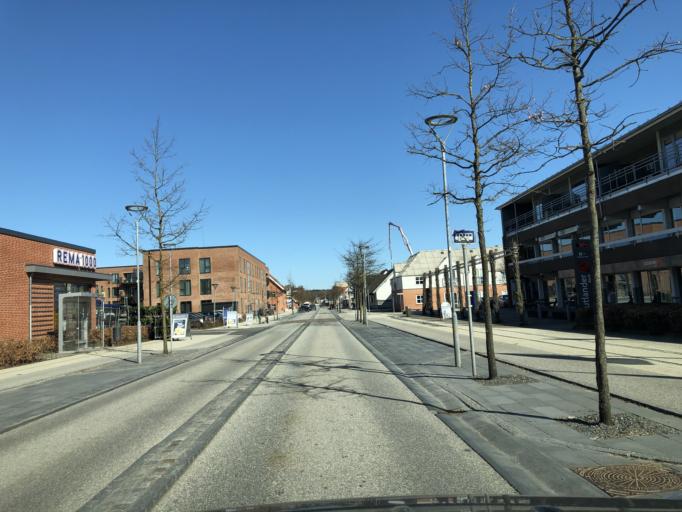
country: DK
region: North Denmark
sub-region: Rebild Kommune
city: Stovring
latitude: 56.8885
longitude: 9.8372
